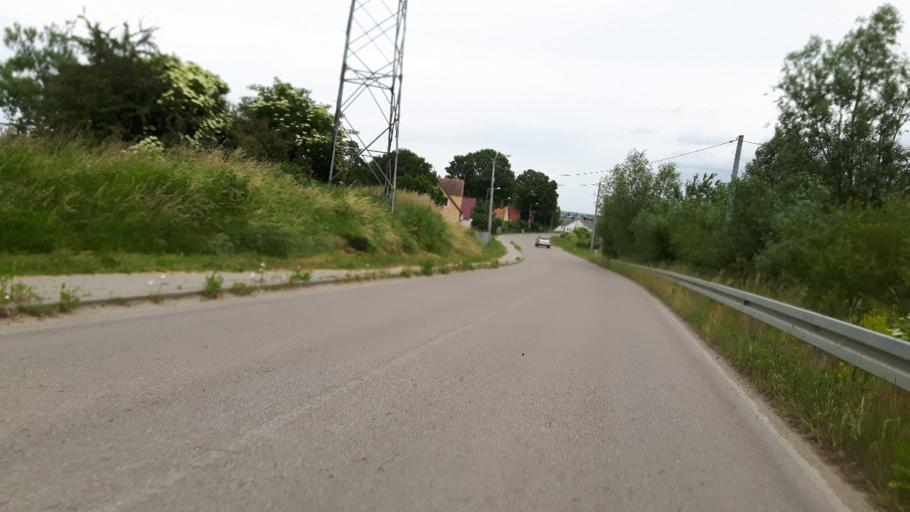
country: PL
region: Warmian-Masurian Voivodeship
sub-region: Powiat elblaski
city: Elblag
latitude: 54.1888
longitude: 19.3168
